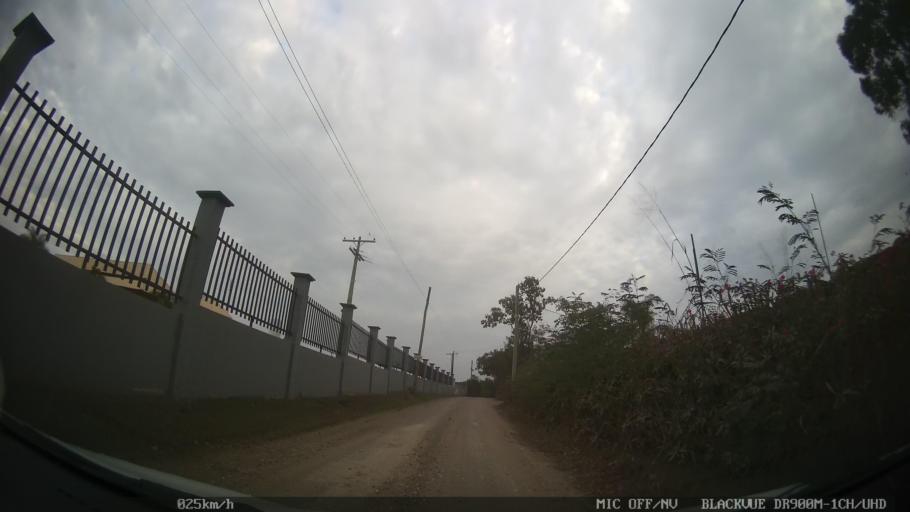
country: BR
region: Sao Paulo
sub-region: Americana
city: Americana
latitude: -22.6644
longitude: -47.3748
